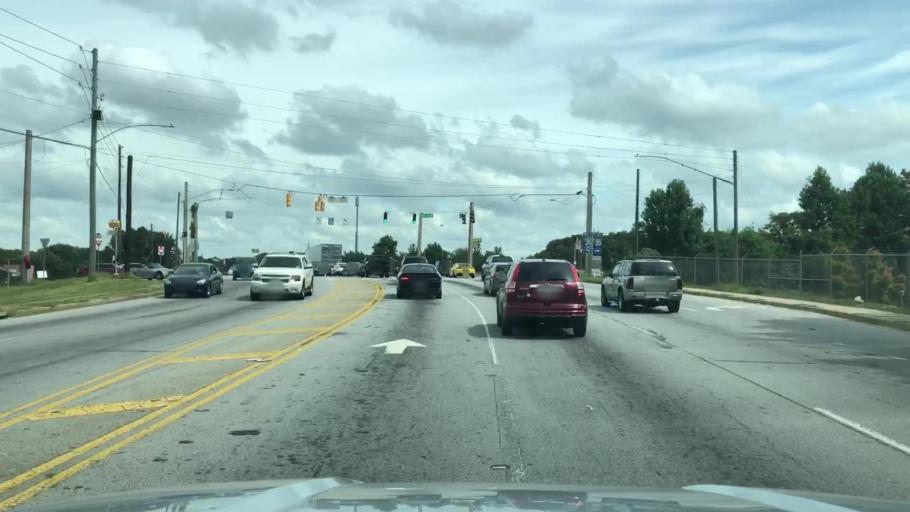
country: US
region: Georgia
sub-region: DeKalb County
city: Redan
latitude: 33.7021
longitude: -84.1709
